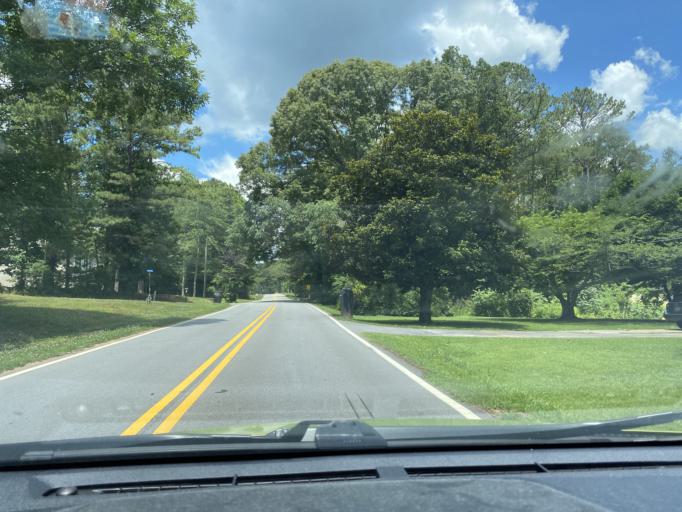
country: US
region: Georgia
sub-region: Fulton County
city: Palmetto
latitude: 33.4339
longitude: -84.6818
